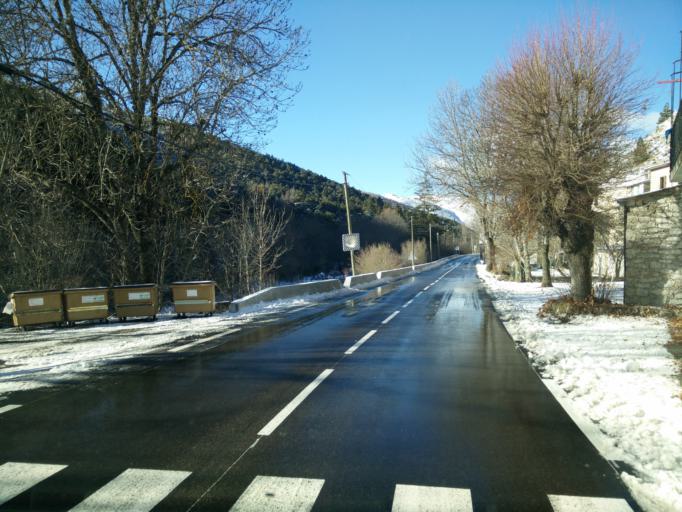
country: FR
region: Provence-Alpes-Cote d'Azur
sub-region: Departement des Alpes-de-Haute-Provence
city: Annot
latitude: 43.9136
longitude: 6.5868
